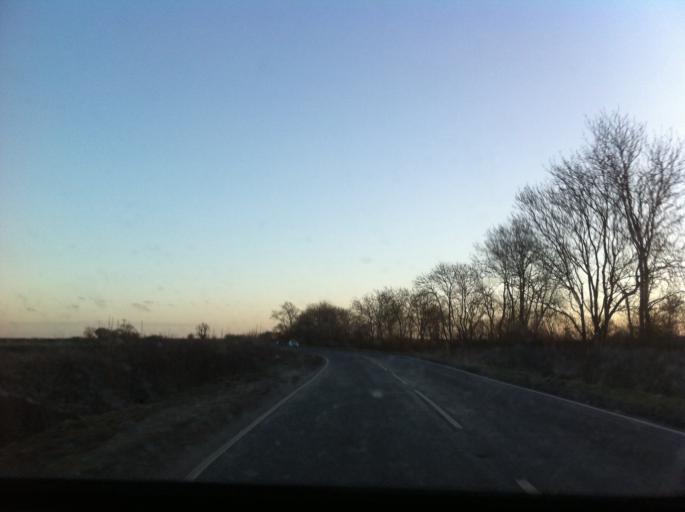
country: GB
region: England
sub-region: Northamptonshire
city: Irchester
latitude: 52.2724
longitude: -0.6549
